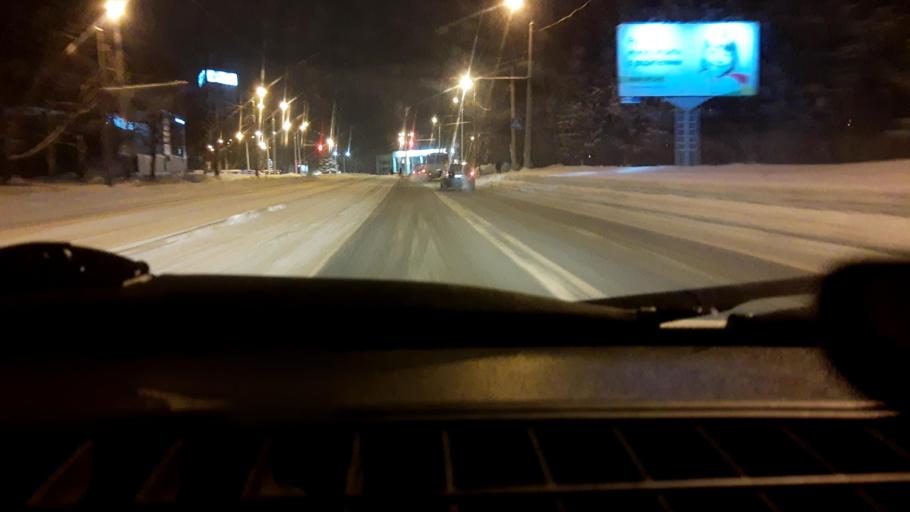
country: RU
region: Bashkortostan
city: Ufa
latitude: 54.7966
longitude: 56.0422
